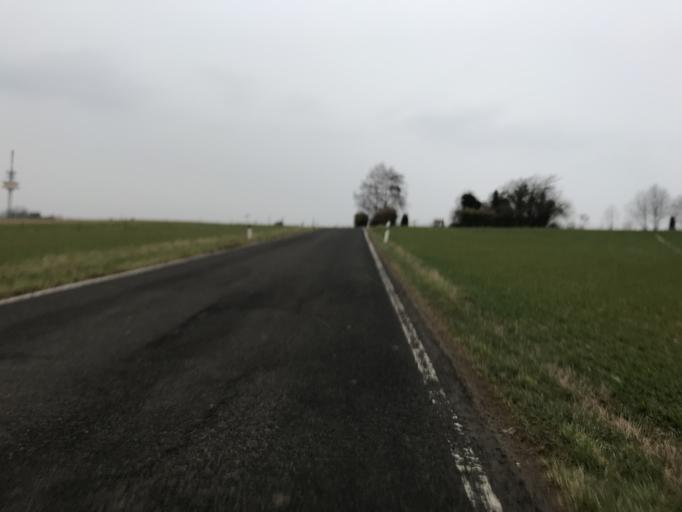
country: DE
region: Rheinland-Pfalz
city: Ober-Olm
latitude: 49.9402
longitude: 8.1848
